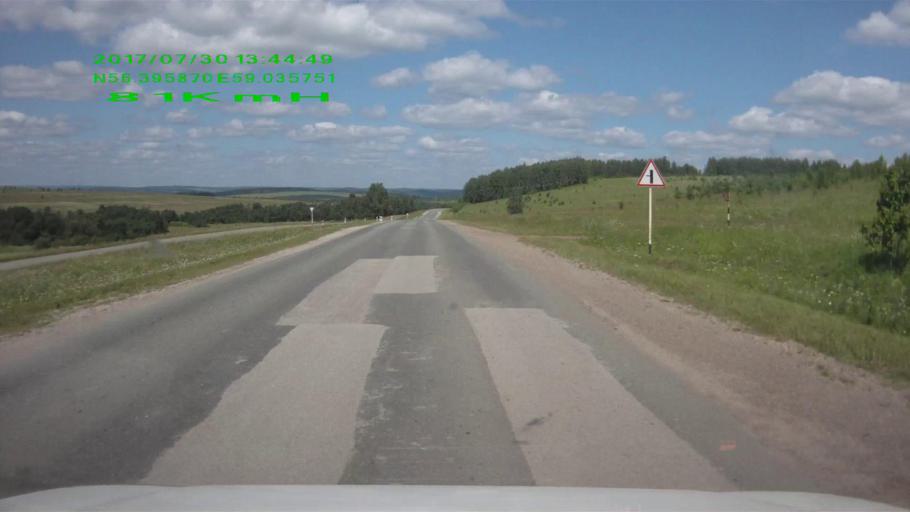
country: RU
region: Sverdlovsk
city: Mikhaylovsk
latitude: 56.3963
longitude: 59.0358
